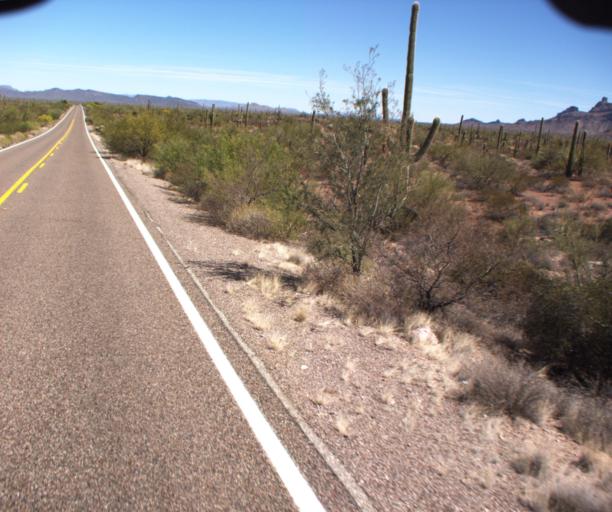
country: MX
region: Sonora
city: Sonoyta
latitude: 32.0867
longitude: -112.7766
